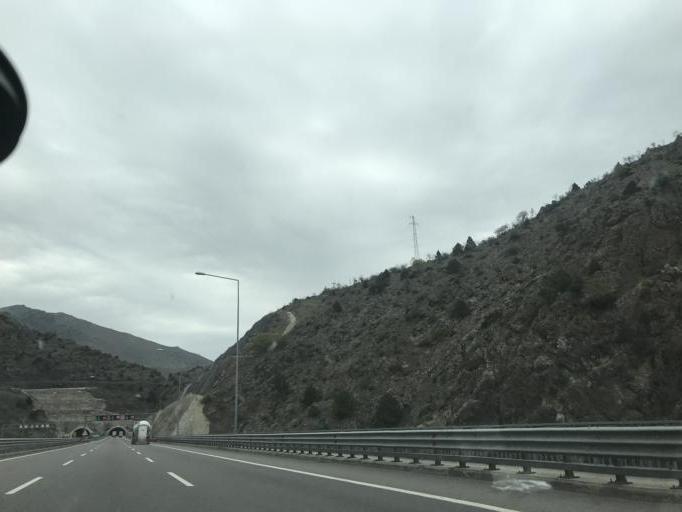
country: TR
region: Nigde
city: Ciftehan
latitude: 37.5550
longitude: 34.7705
